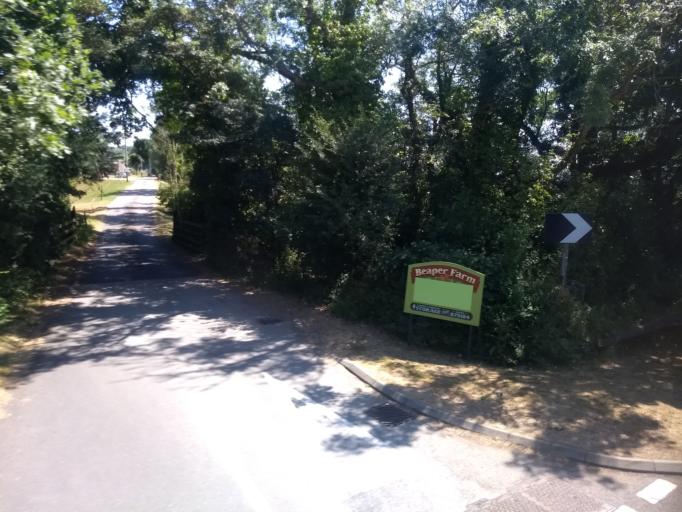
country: GB
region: England
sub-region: Isle of Wight
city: Brading
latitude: 50.6989
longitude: -1.1445
